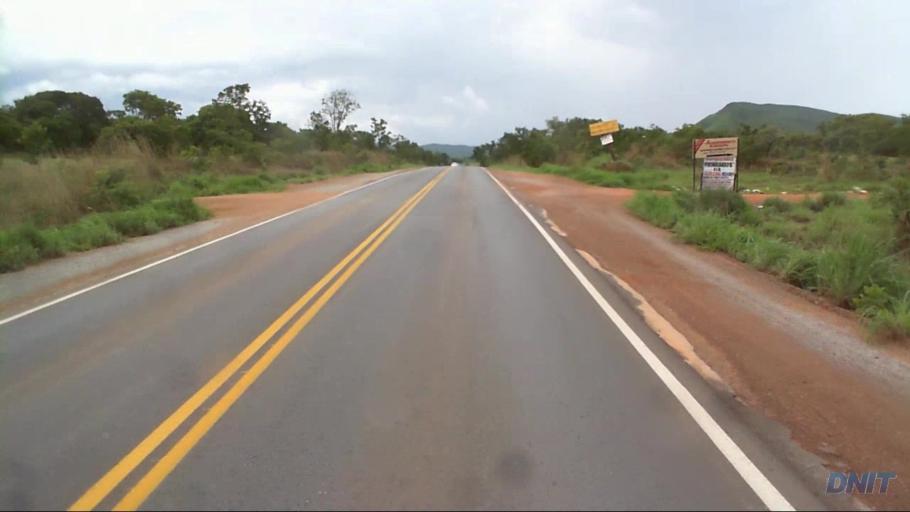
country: BR
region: Goias
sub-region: Padre Bernardo
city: Padre Bernardo
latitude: -15.4036
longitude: -48.2000
